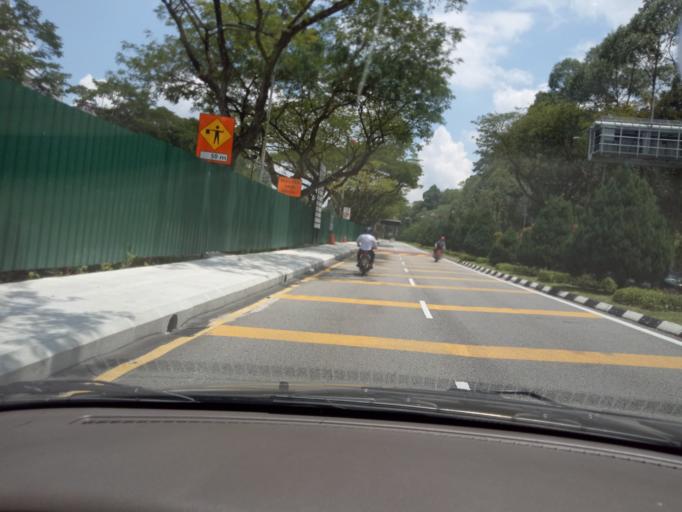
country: MY
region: Kuala Lumpur
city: Kuala Lumpur
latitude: 3.1504
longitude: 101.6888
